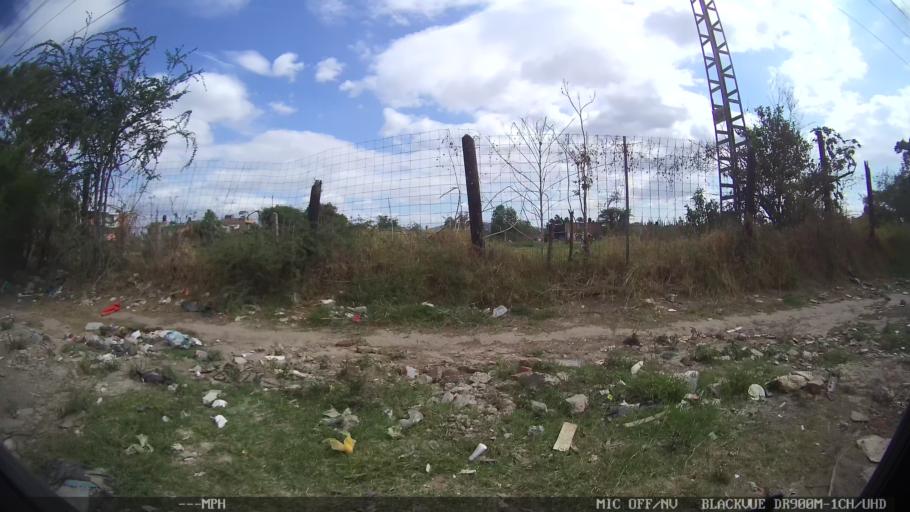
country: MX
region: Jalisco
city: Tonala
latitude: 20.6661
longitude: -103.2506
